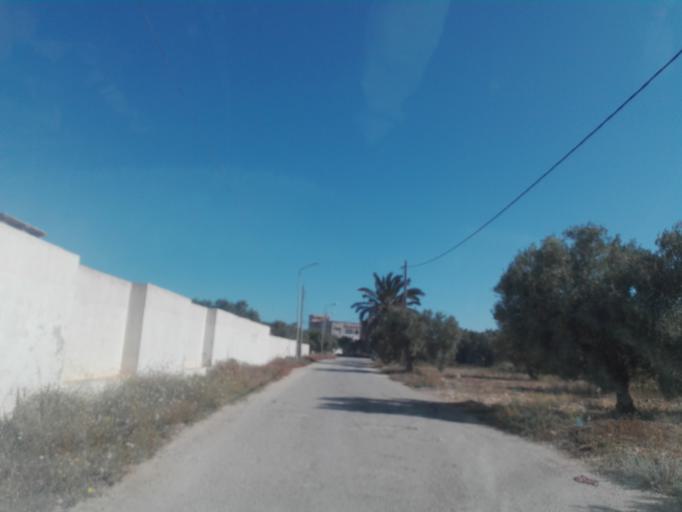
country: TN
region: Safaqis
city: Al Qarmadah
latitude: 34.7096
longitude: 11.2027
